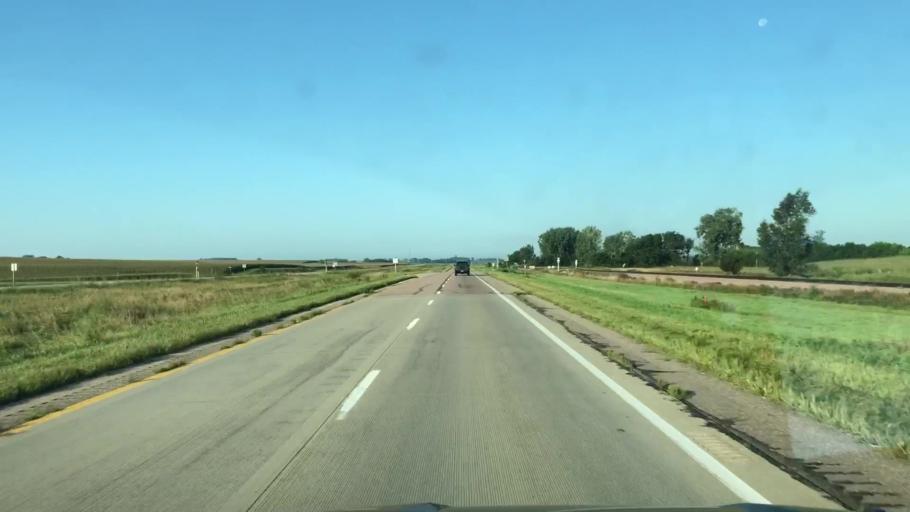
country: US
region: Iowa
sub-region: Sioux County
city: Alton
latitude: 43.0268
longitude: -95.9405
